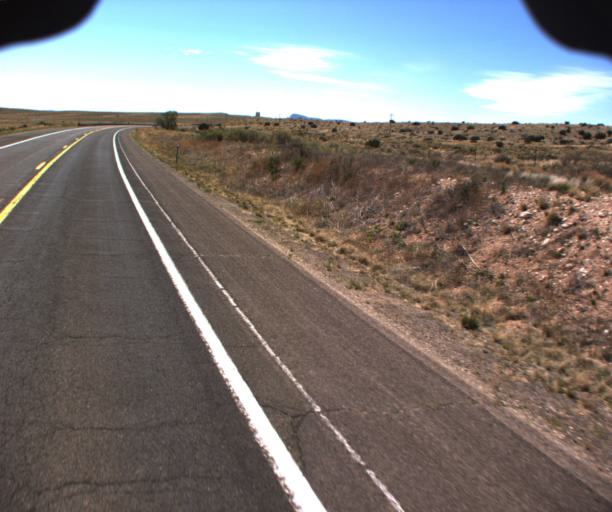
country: US
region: Arizona
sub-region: Mohave County
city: Peach Springs
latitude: 35.5225
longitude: -113.4488
